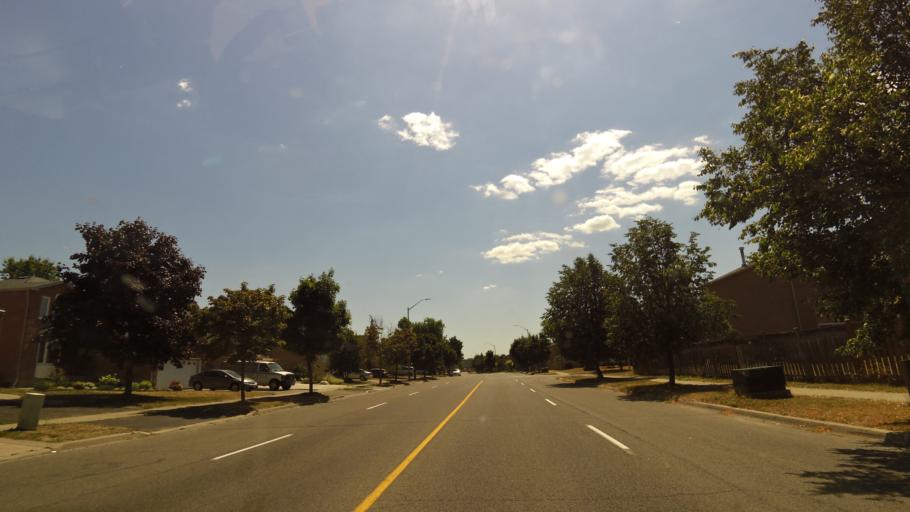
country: CA
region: Ontario
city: Brampton
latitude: 43.6364
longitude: -79.8764
